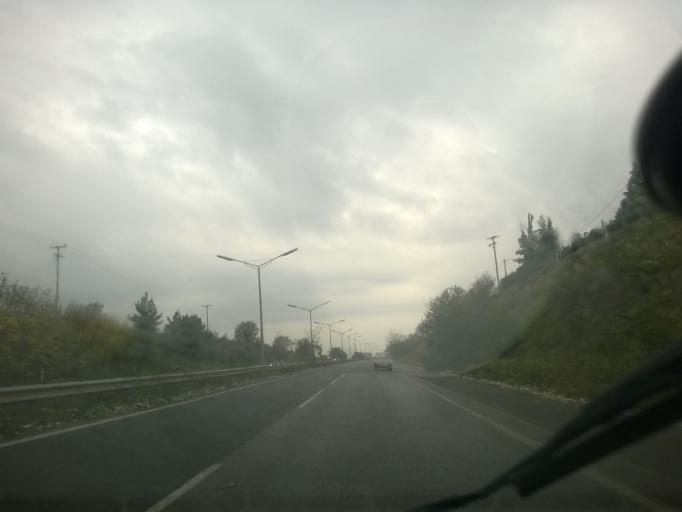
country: GR
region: Central Macedonia
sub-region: Nomos Thessalonikis
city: Agios Athanasios
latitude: 40.7105
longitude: 22.7604
